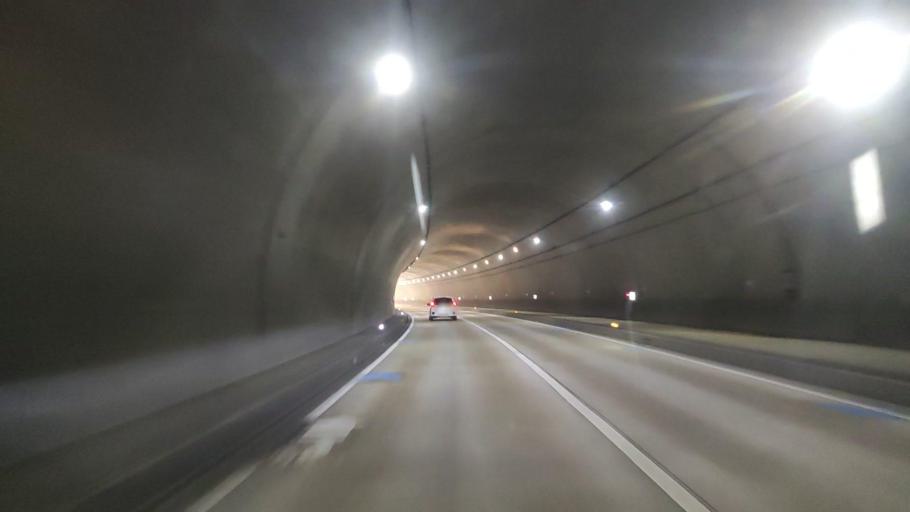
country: JP
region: Wakayama
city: Shingu
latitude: 33.7383
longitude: 135.9897
